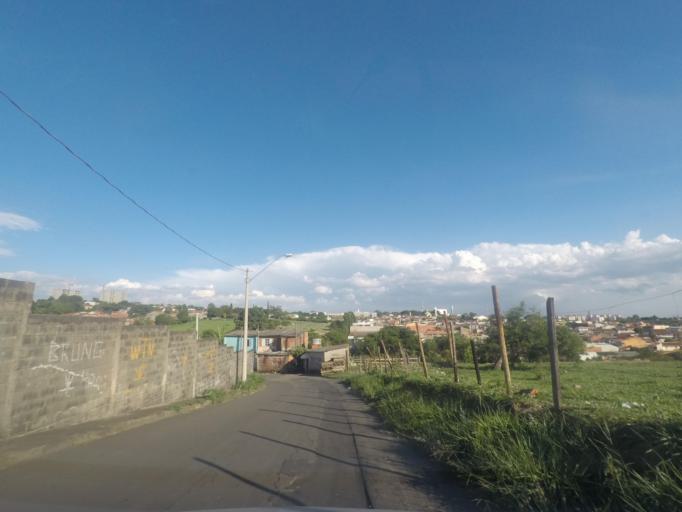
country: BR
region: Sao Paulo
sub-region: Sumare
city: Sumare
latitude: -22.8097
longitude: -47.2549
